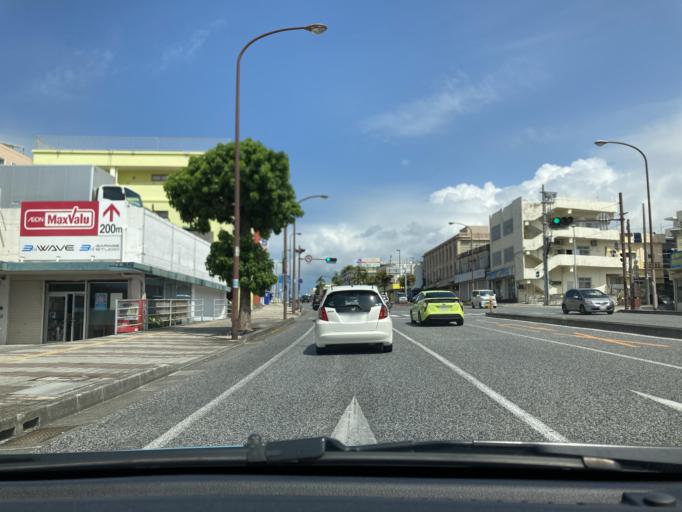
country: JP
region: Okinawa
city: Okinawa
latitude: 26.3218
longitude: 127.7932
